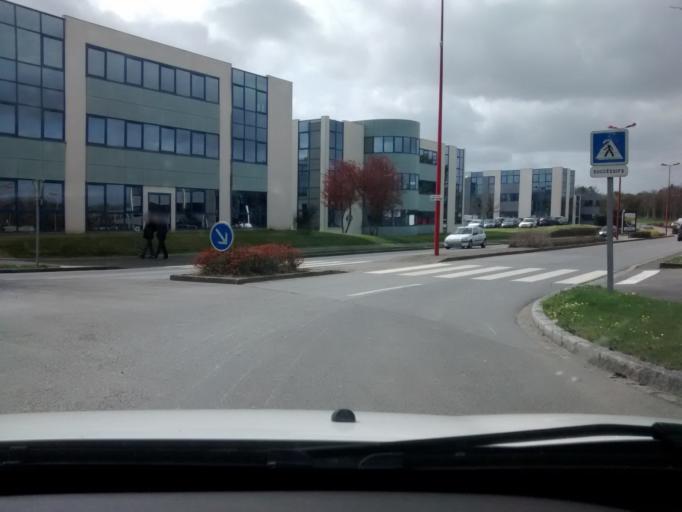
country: FR
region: Brittany
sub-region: Departement d'Ille-et-Vilaine
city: Saint-Gregoire
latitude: 48.1549
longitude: -1.6969
